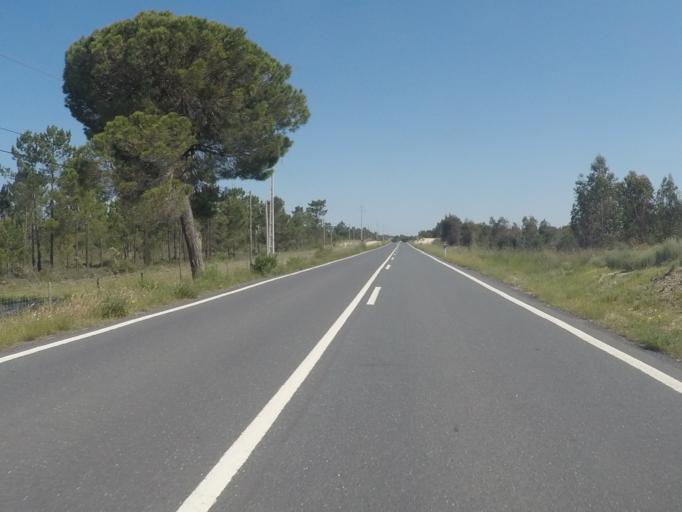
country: PT
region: Setubal
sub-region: Grandola
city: Grandola
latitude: 38.2423
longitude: -8.7374
